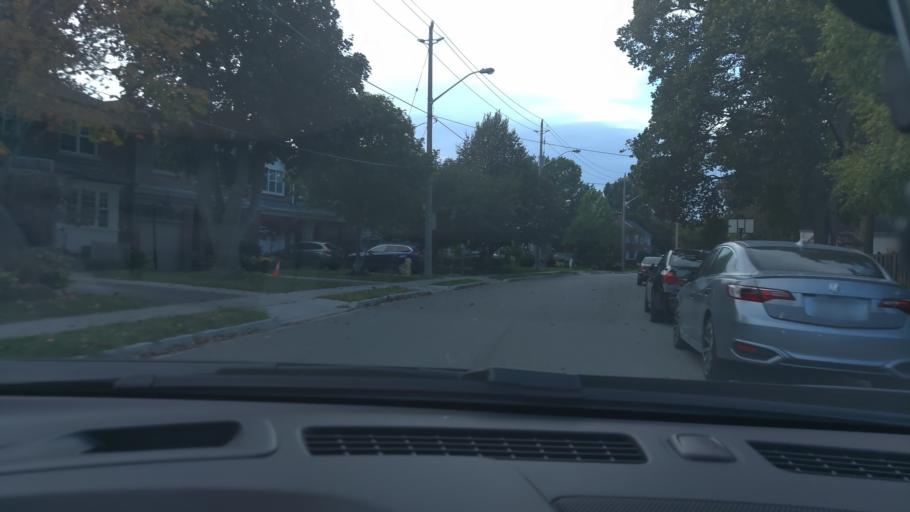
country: CA
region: Ontario
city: Toronto
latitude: 43.7179
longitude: -79.3651
